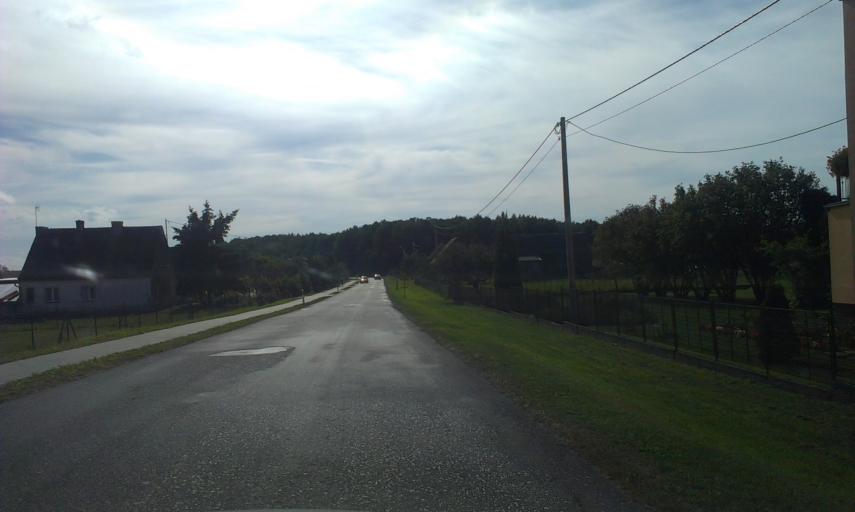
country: PL
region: Greater Poland Voivodeship
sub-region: Powiat zlotowski
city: Zlotow
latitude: 53.4176
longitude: 16.9863
